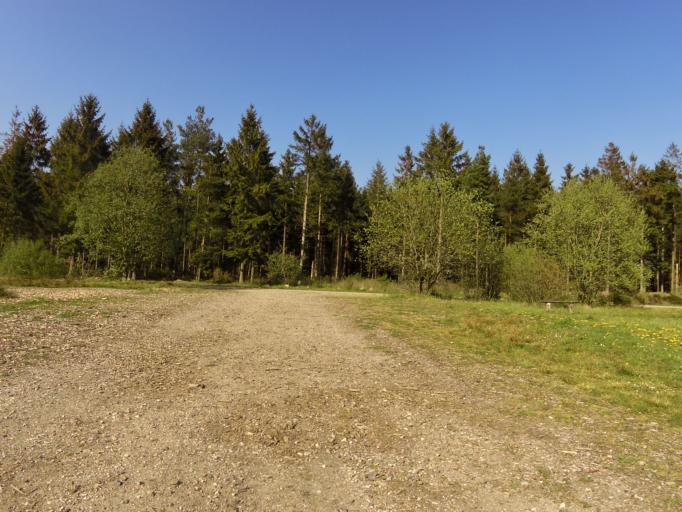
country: DK
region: South Denmark
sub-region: Tonder Kommune
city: Logumkloster
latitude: 55.1808
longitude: 8.9369
